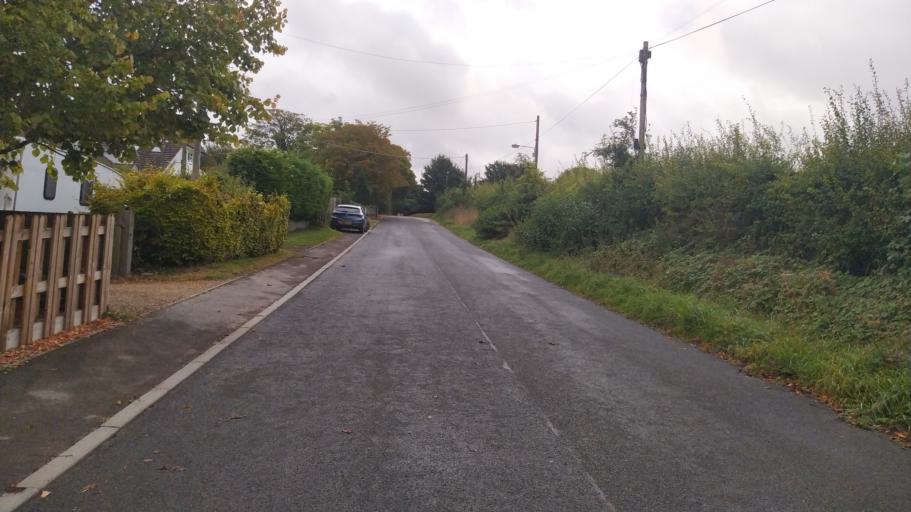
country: GB
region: England
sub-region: Wiltshire
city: Allington
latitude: 51.1166
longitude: -1.7166
